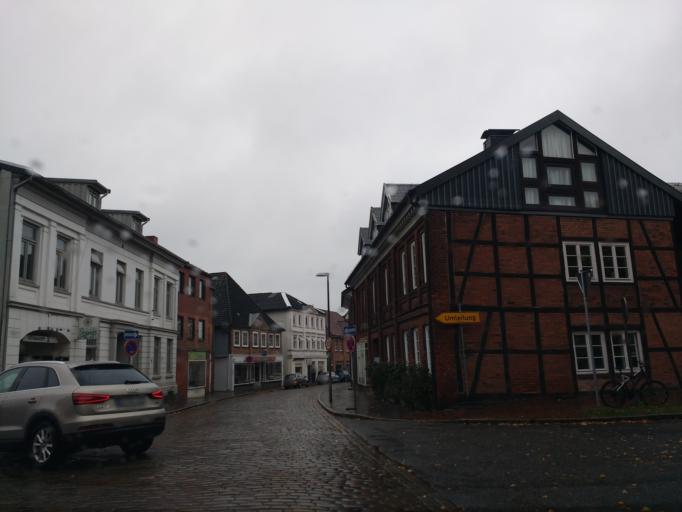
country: DE
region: Schleswig-Holstein
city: Eutin
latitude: 54.1339
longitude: 10.6175
